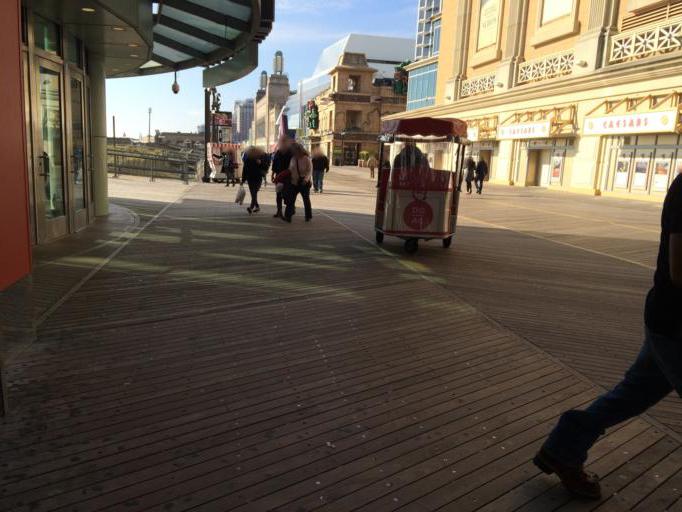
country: US
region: New Jersey
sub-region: Atlantic County
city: Atlantic City
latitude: 39.3548
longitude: -74.4349
